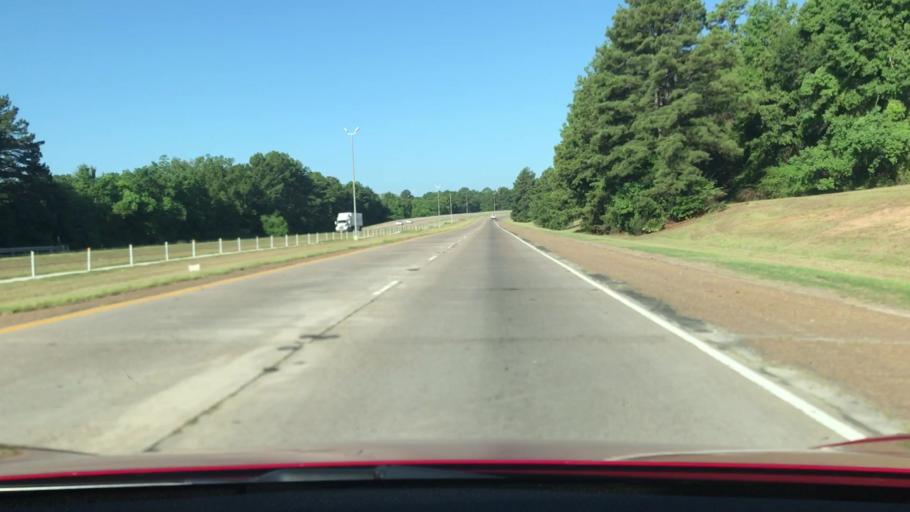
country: US
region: Louisiana
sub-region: Bossier Parish
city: Bossier City
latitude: 32.4178
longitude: -93.7807
